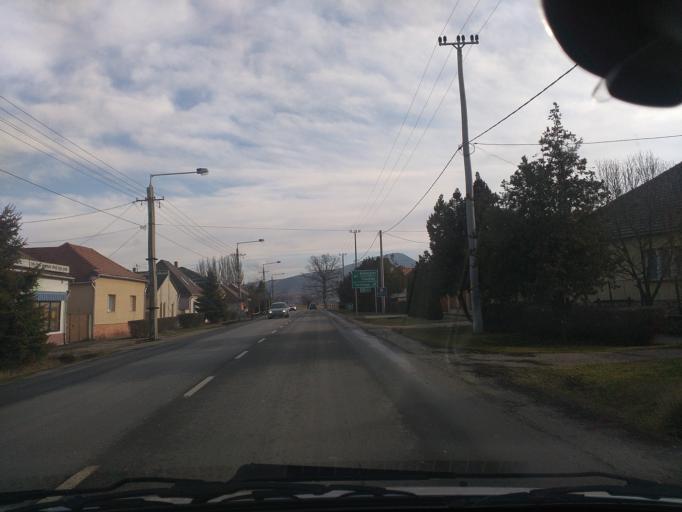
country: HU
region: Komarom-Esztergom
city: Tat
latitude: 47.7414
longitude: 18.6502
